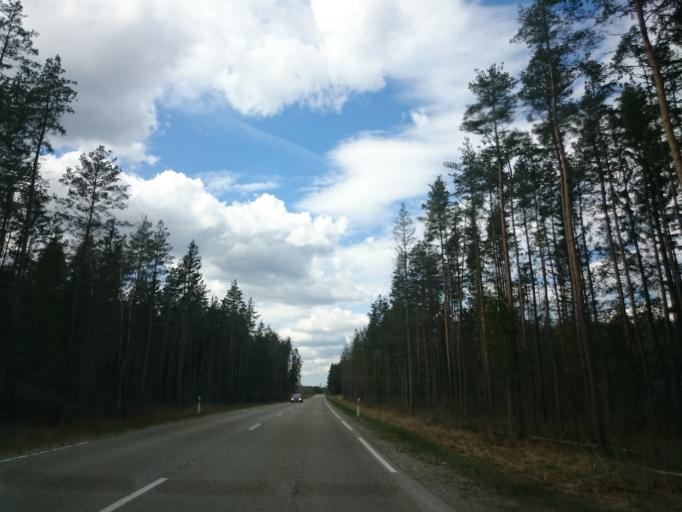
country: LV
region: Kuldigas Rajons
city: Kuldiga
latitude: 56.9512
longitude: 22.2557
